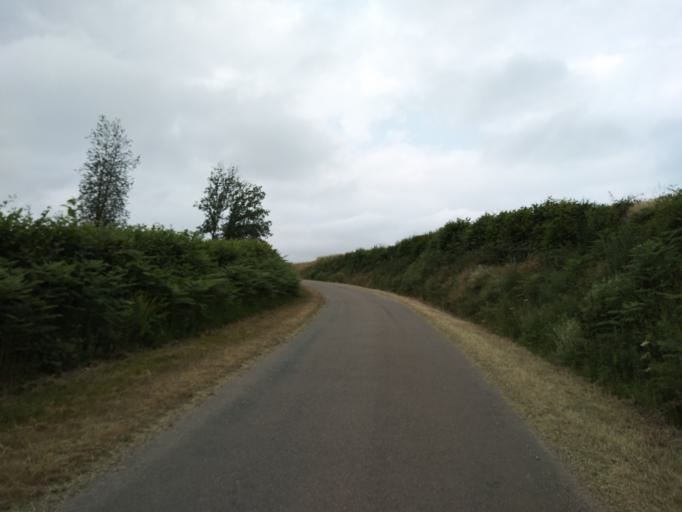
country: FR
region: Bourgogne
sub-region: Departement de la Cote-d'Or
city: Saulieu
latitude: 47.2858
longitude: 4.1260
